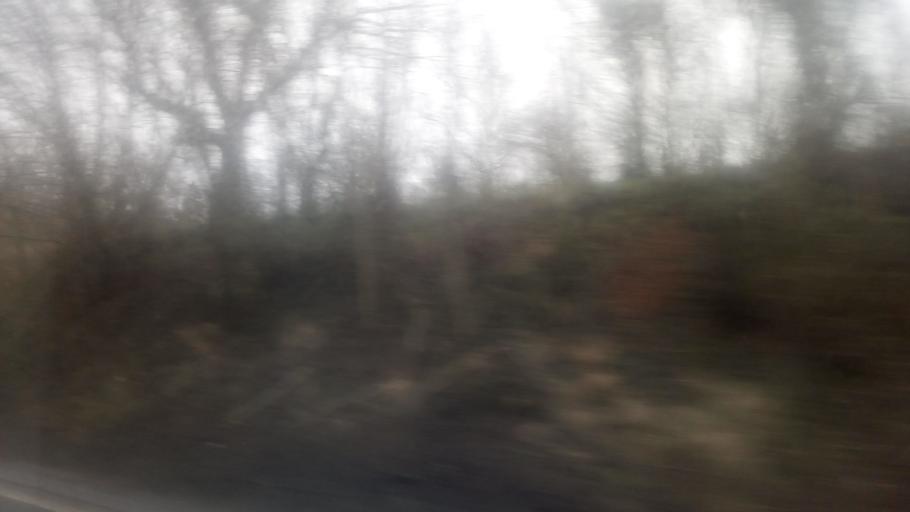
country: GB
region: Scotland
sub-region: The Scottish Borders
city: Newtown St Boswells
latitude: 55.5918
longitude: -2.6702
